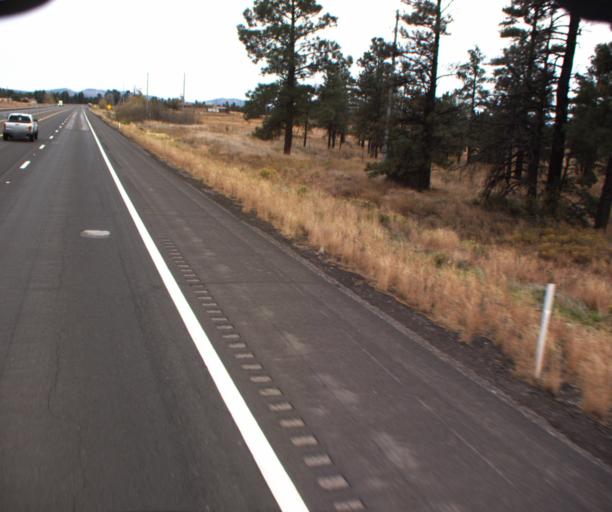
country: US
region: Arizona
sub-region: Coconino County
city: Flagstaff
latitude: 35.3378
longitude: -111.5541
